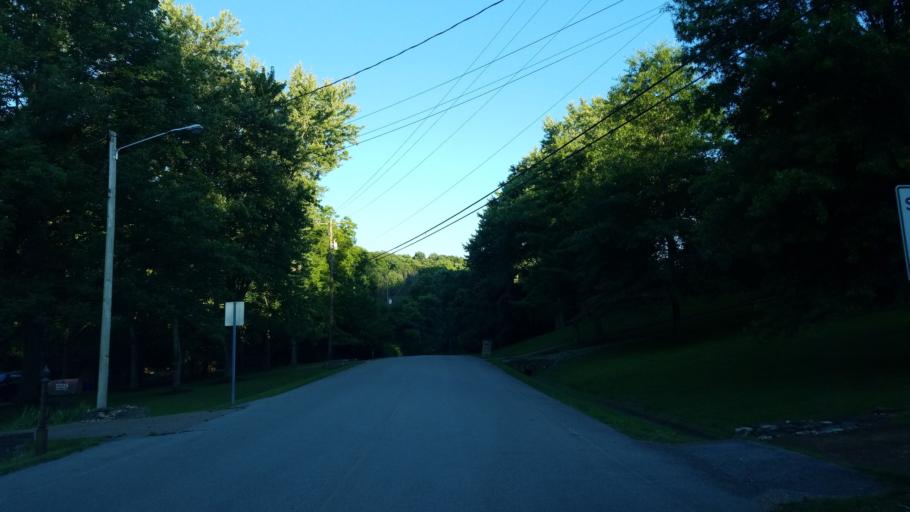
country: US
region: Tennessee
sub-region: Williamson County
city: Brentwood
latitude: 36.0471
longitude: -86.7920
